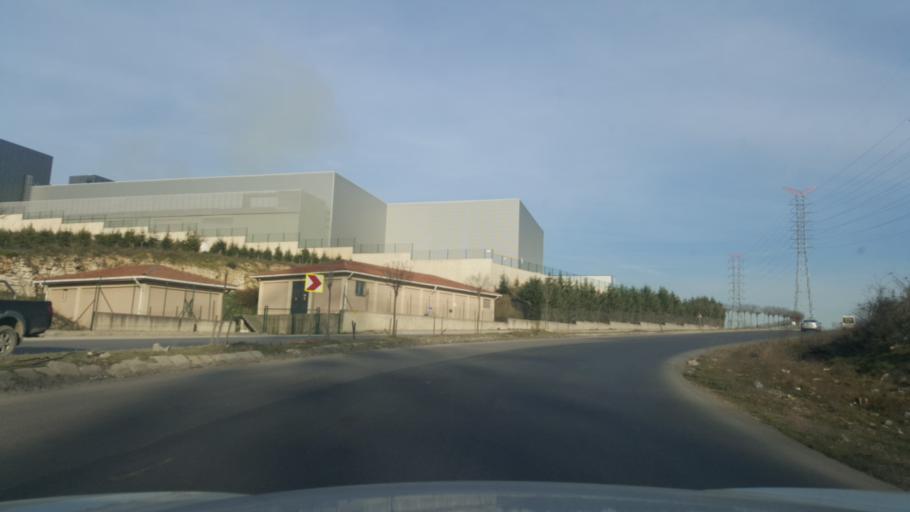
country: TR
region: Kocaeli
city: Tavsancil
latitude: 40.8088
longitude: 29.5600
